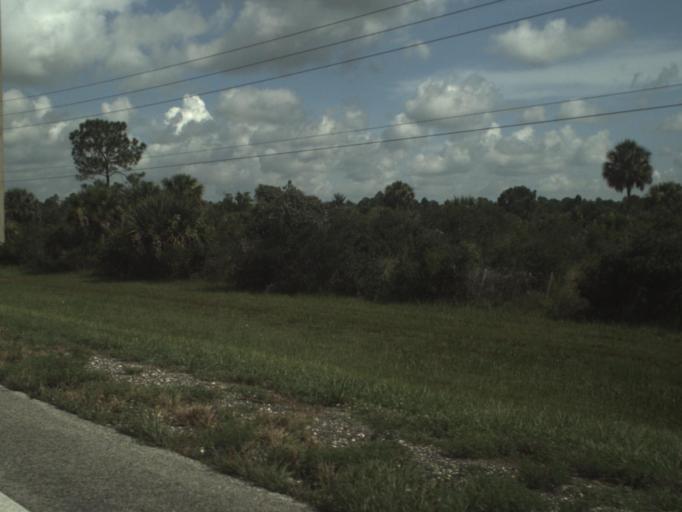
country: US
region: Florida
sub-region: Palm Beach County
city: Palm Beach Gardens
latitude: 26.8471
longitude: -80.2078
